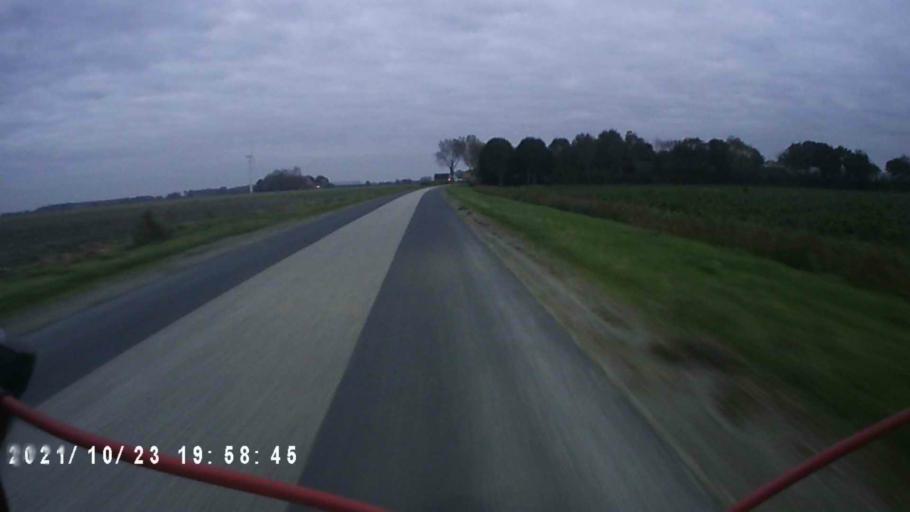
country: NL
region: Friesland
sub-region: Gemeente Harlingen
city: Harlingen
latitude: 53.1122
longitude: 5.4535
